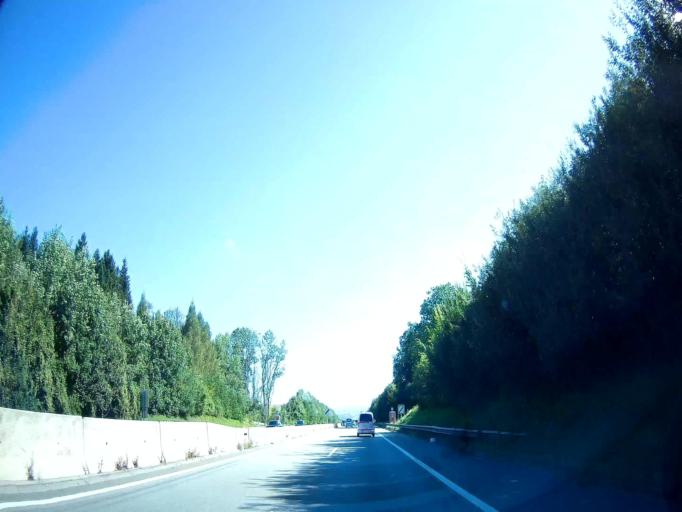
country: AT
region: Upper Austria
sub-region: Wels-Land
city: Sattledt
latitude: 48.0040
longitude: 14.0764
